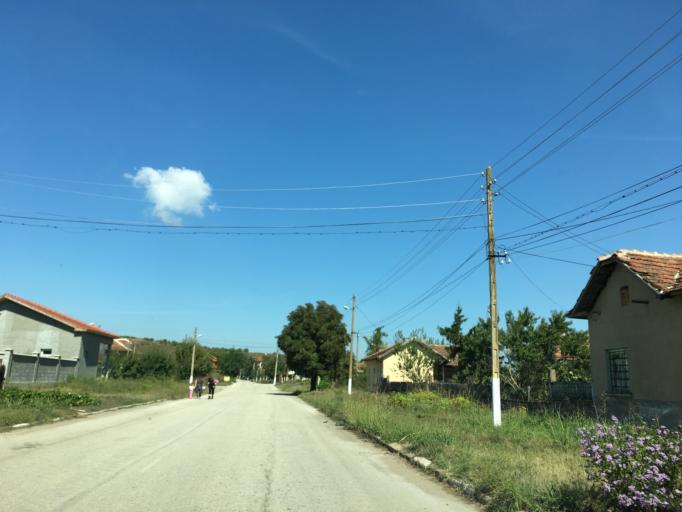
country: RO
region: Olt
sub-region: Comuna Orlea
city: Orlea
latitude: 43.6431
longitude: 24.3997
